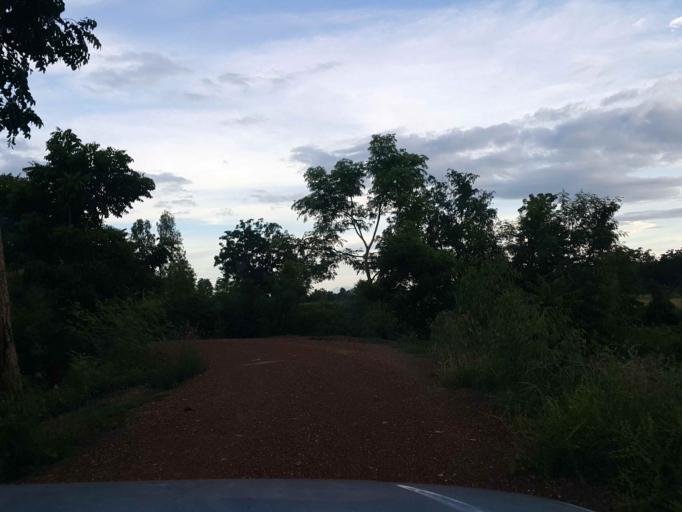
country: TH
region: Sukhothai
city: Sawankhalok
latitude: 17.3413
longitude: 99.7438
